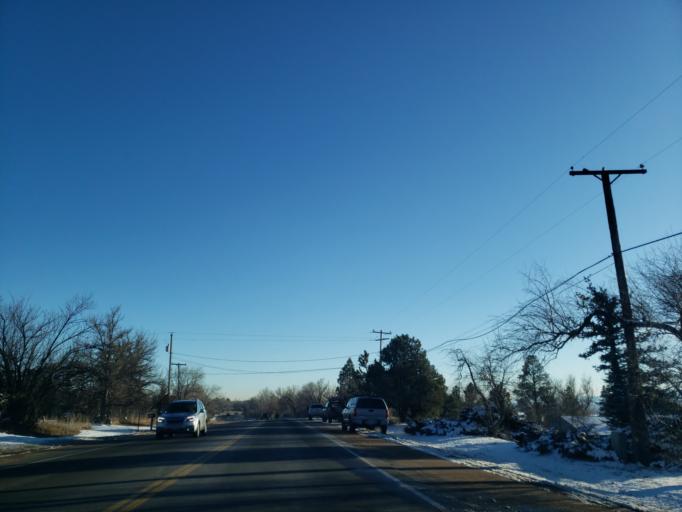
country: US
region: Colorado
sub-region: Larimer County
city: Fort Collins
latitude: 40.6348
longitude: -105.0722
